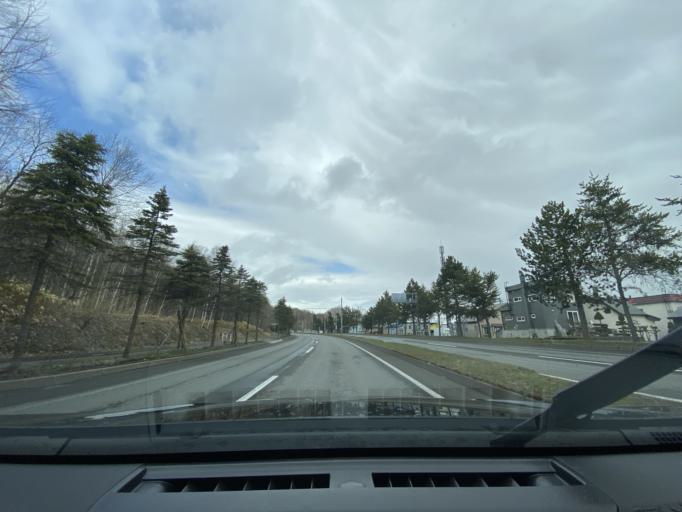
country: JP
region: Hokkaido
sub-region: Asahikawa-shi
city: Asahikawa
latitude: 43.7996
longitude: 142.3399
